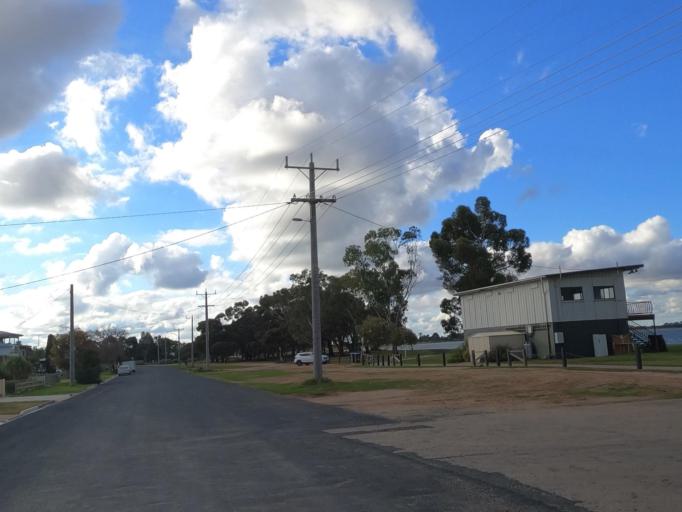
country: AU
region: Victoria
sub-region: Swan Hill
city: Swan Hill
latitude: -35.4500
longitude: 143.6276
